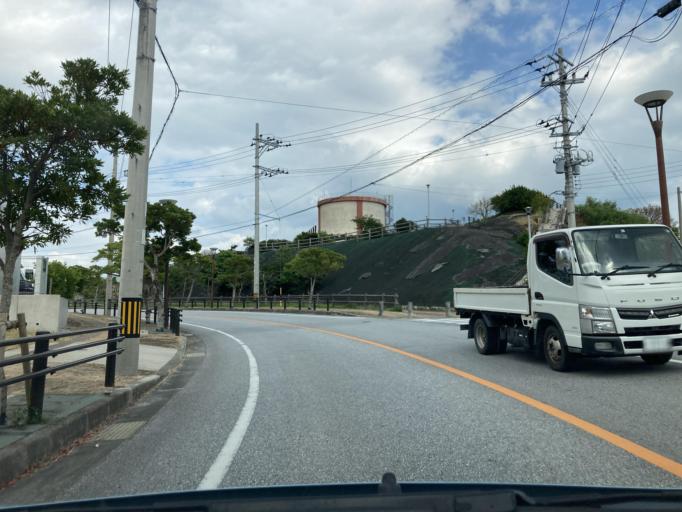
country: JP
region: Okinawa
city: Ginowan
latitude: 26.2461
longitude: 127.7718
